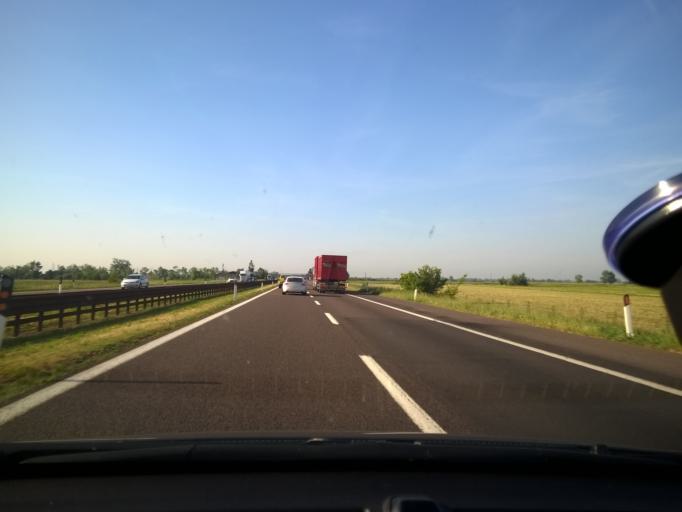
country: IT
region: Emilia-Romagna
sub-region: Provincia di Modena
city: Migliarina
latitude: 44.8440
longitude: 10.8518
